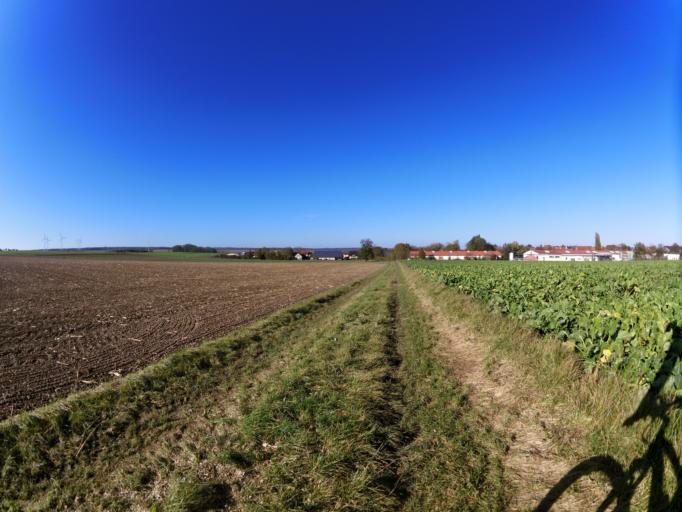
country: DE
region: Bavaria
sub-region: Regierungsbezirk Unterfranken
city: Geroldshausen
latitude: 49.6890
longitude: 9.9302
